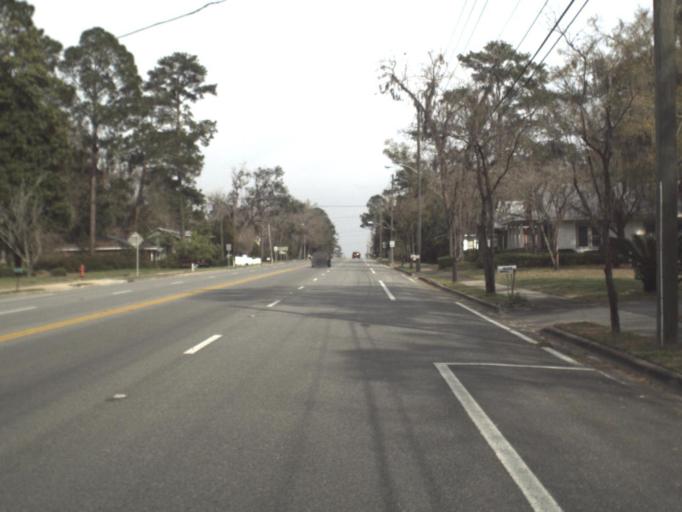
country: US
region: Florida
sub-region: Jefferson County
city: Monticello
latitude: 30.5451
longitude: -83.8598
